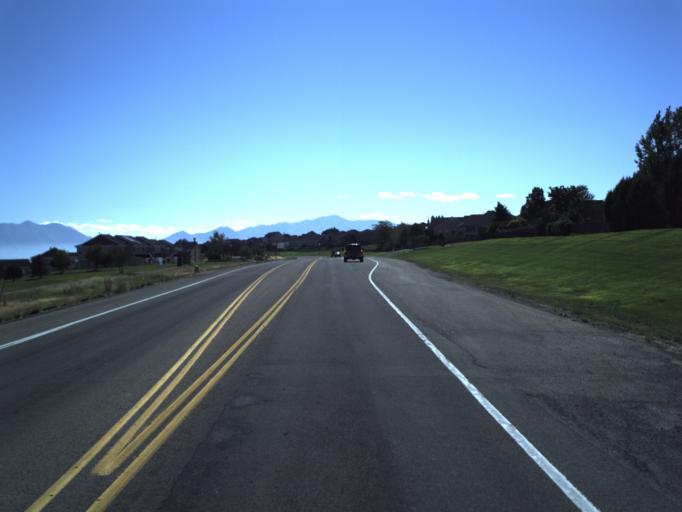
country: US
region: Utah
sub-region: Utah County
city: Saratoga Springs
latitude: 40.3216
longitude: -111.9019
